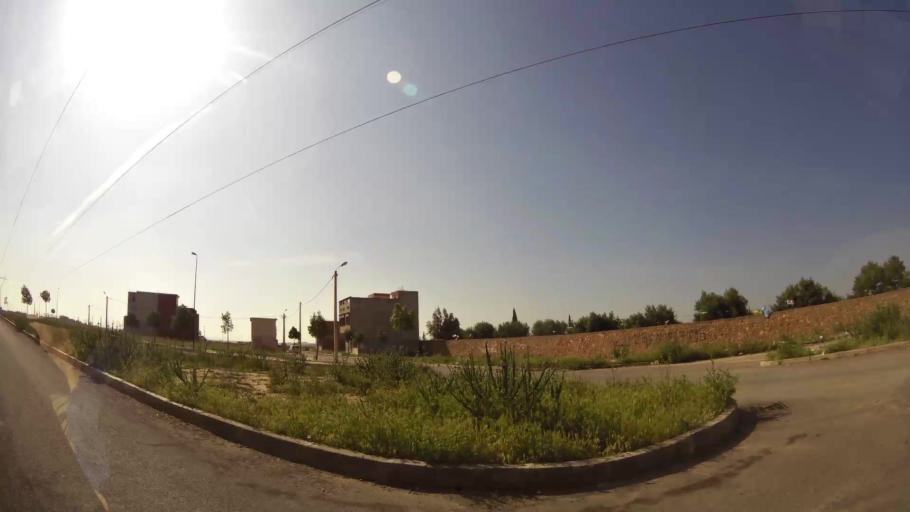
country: MA
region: Oriental
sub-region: Oujda-Angad
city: Oujda
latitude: 34.7250
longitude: -1.8804
